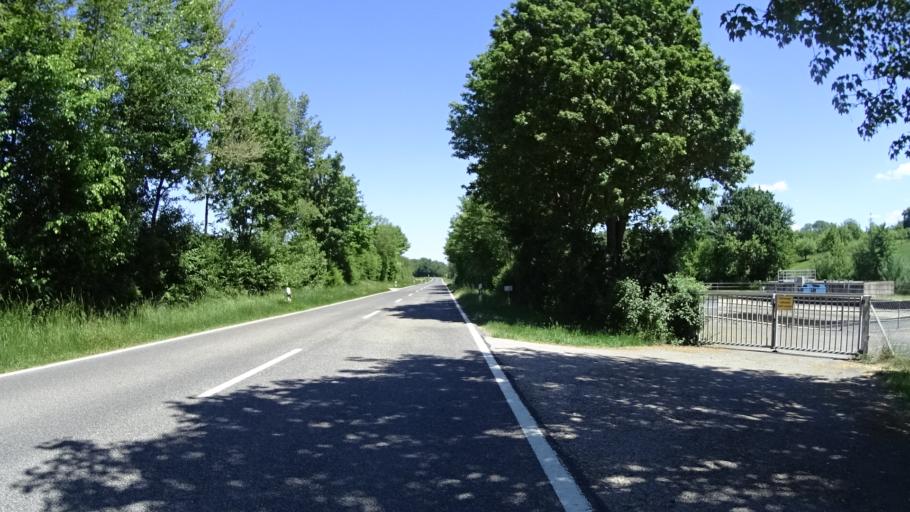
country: DE
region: Bavaria
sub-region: Regierungsbezirk Mittelfranken
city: Heideck
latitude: 49.1021
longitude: 11.1392
